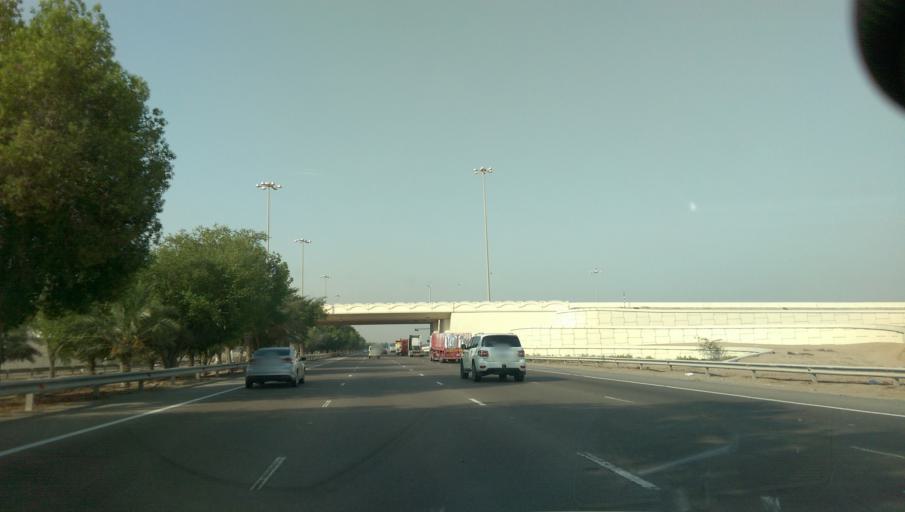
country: AE
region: Abu Dhabi
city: Abu Dhabi
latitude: 24.3704
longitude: 54.6548
